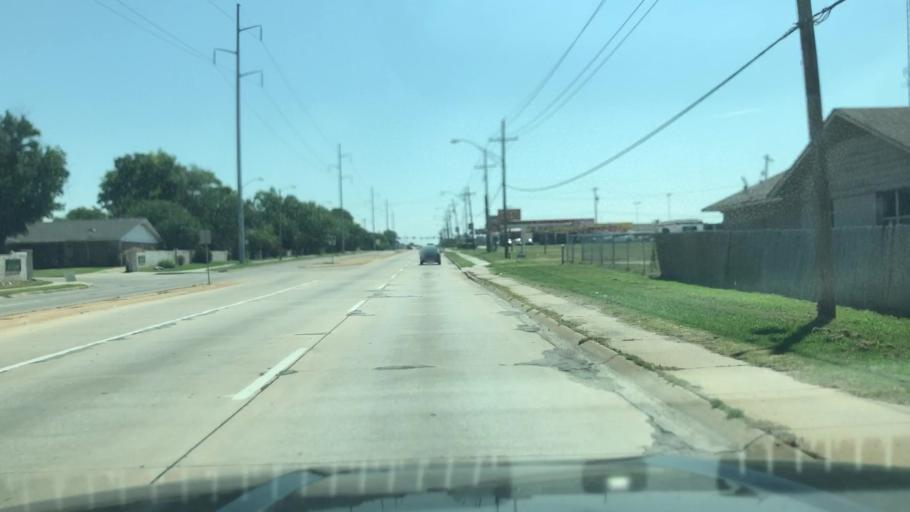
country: US
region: Oklahoma
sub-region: Tulsa County
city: Broken Arrow
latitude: 36.1334
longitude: -95.8566
